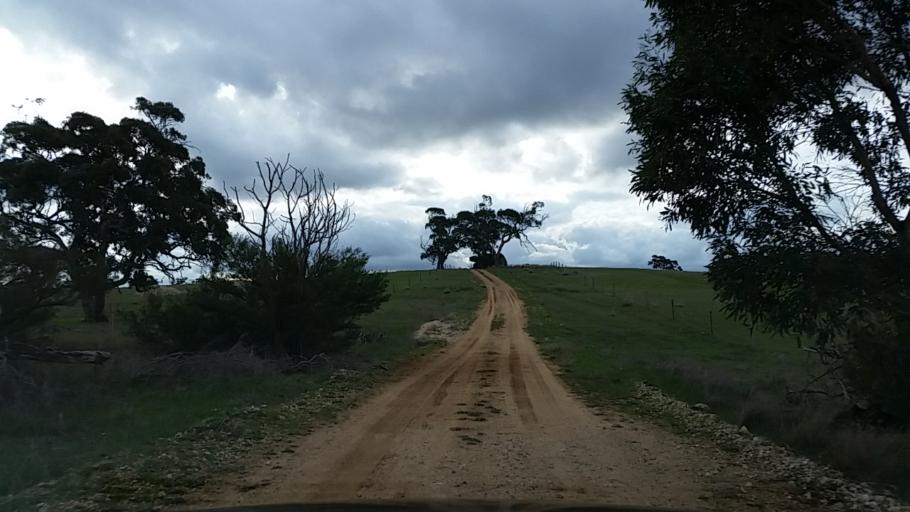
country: AU
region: South Australia
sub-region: Mount Barker
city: Callington
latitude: -34.9643
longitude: 139.0542
